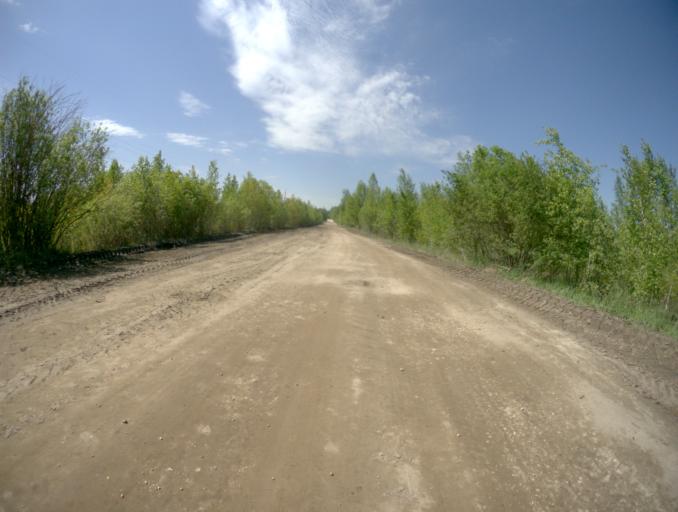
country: RU
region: Vladimir
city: Gusevskiy
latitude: 55.6882
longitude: 40.5194
